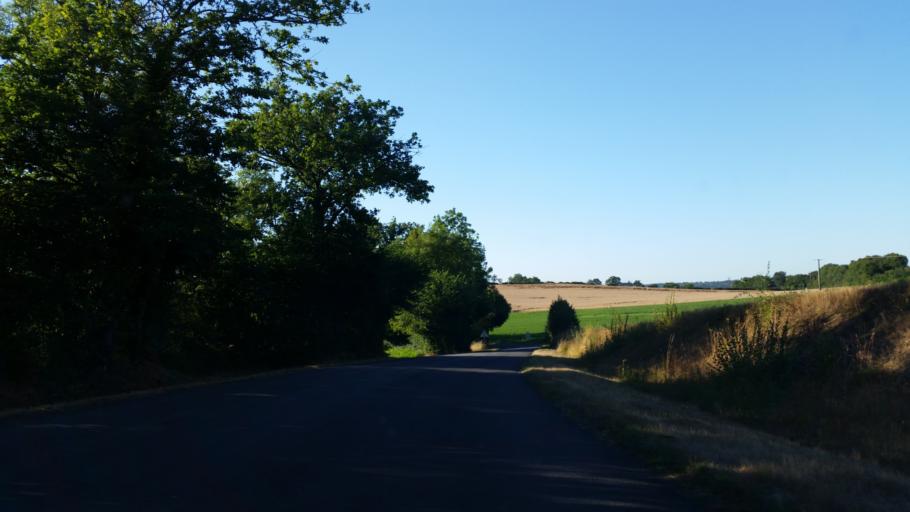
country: FR
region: Lower Normandy
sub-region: Departement de l'Orne
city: Briouze
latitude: 48.8296
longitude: -0.3812
